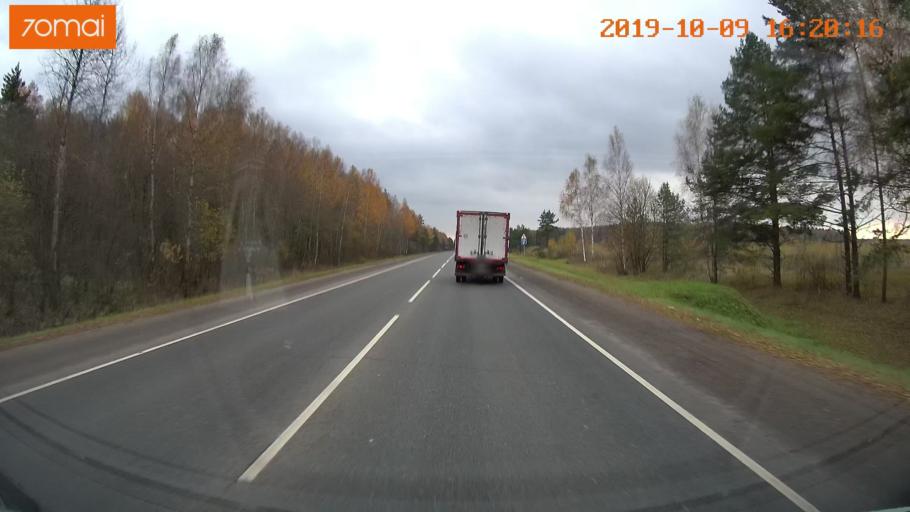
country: RU
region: Kostroma
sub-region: Kostromskoy Rayon
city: Kostroma
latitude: 57.7086
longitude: 40.8926
